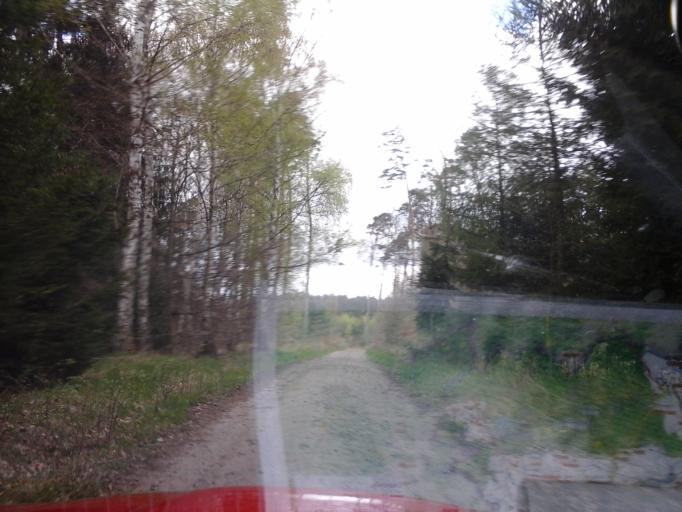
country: PL
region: West Pomeranian Voivodeship
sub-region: Powiat choszczenski
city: Bierzwnik
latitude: 53.0363
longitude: 15.6264
